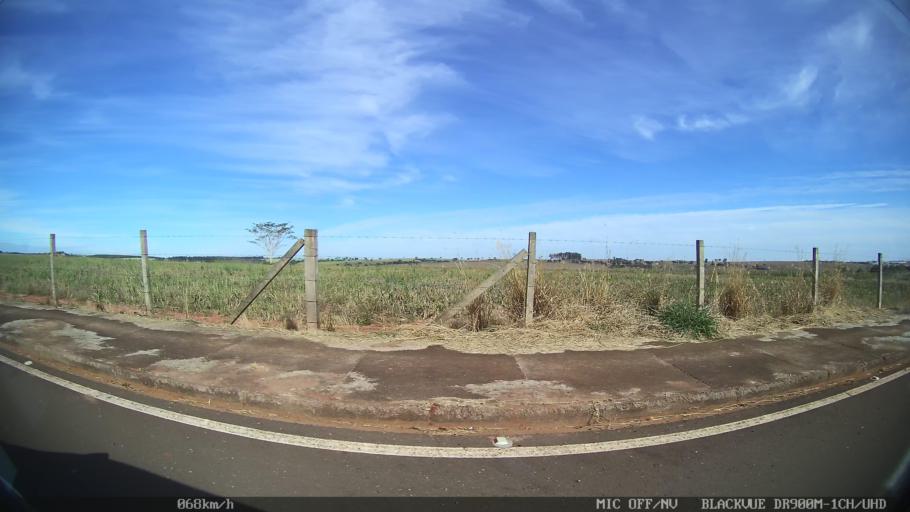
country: BR
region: Sao Paulo
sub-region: Sao Jose Do Rio Preto
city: Sao Jose do Rio Preto
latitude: -20.7931
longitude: -49.3048
